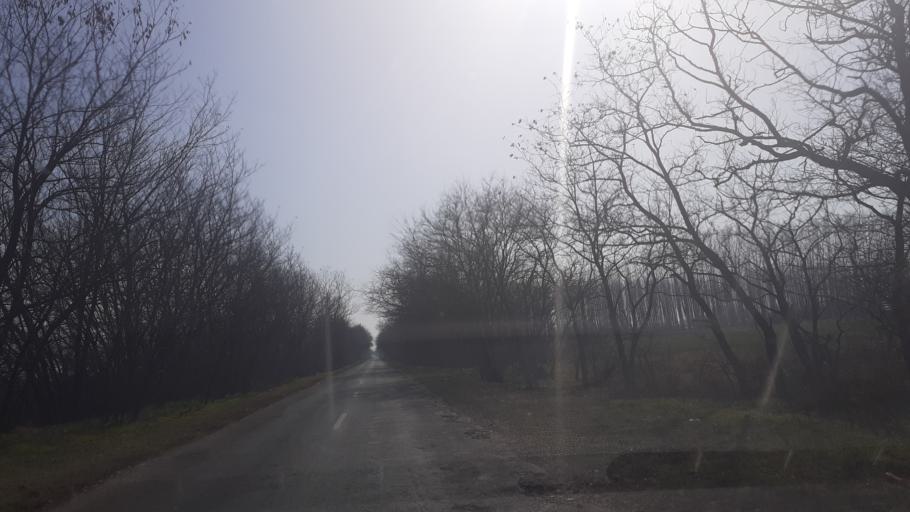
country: HU
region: Pest
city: Orkeny
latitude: 47.0939
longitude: 19.3610
